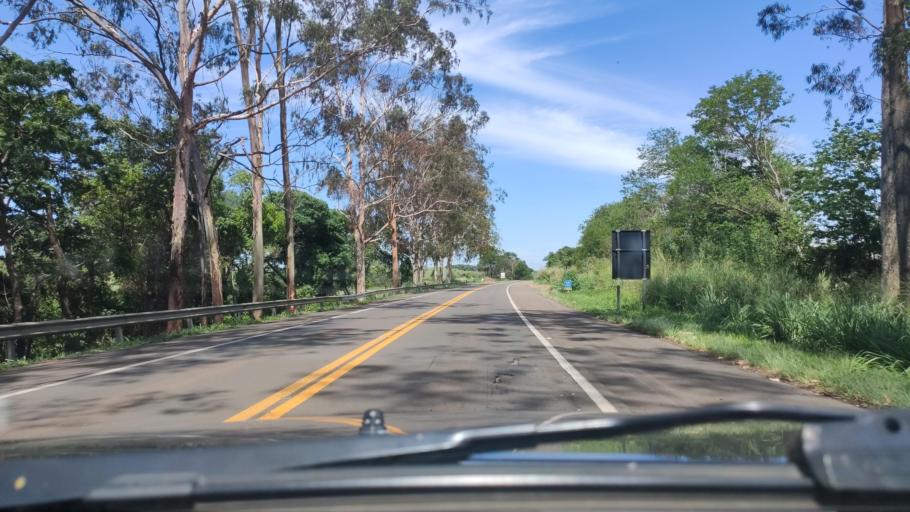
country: BR
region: Sao Paulo
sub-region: Sao Carlos
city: Sao Carlos
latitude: -22.0671
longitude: -47.9033
